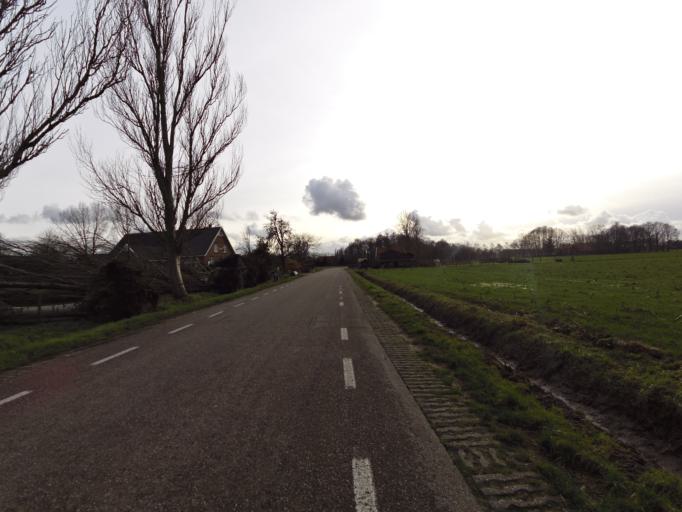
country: NL
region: Gelderland
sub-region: Oude IJsselstreek
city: Wisch
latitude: 51.9723
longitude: 6.4194
